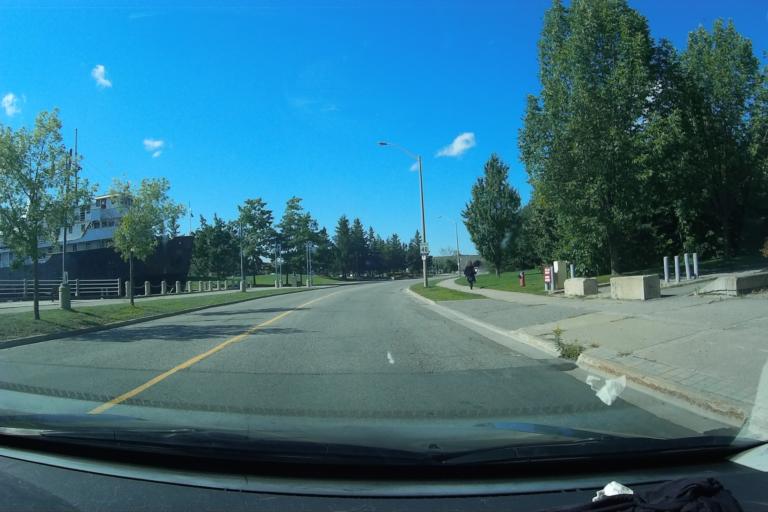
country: CA
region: Ontario
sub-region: Algoma
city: Sault Ste. Marie
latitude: 46.5084
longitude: -84.3347
